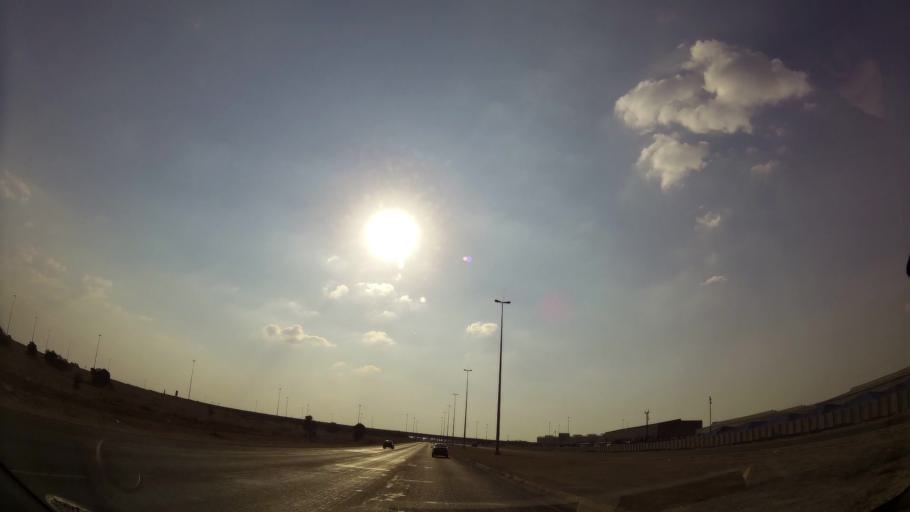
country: ZA
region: Gauteng
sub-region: City of Johannesburg Metropolitan Municipality
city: Modderfontein
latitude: -26.1058
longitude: 28.2577
